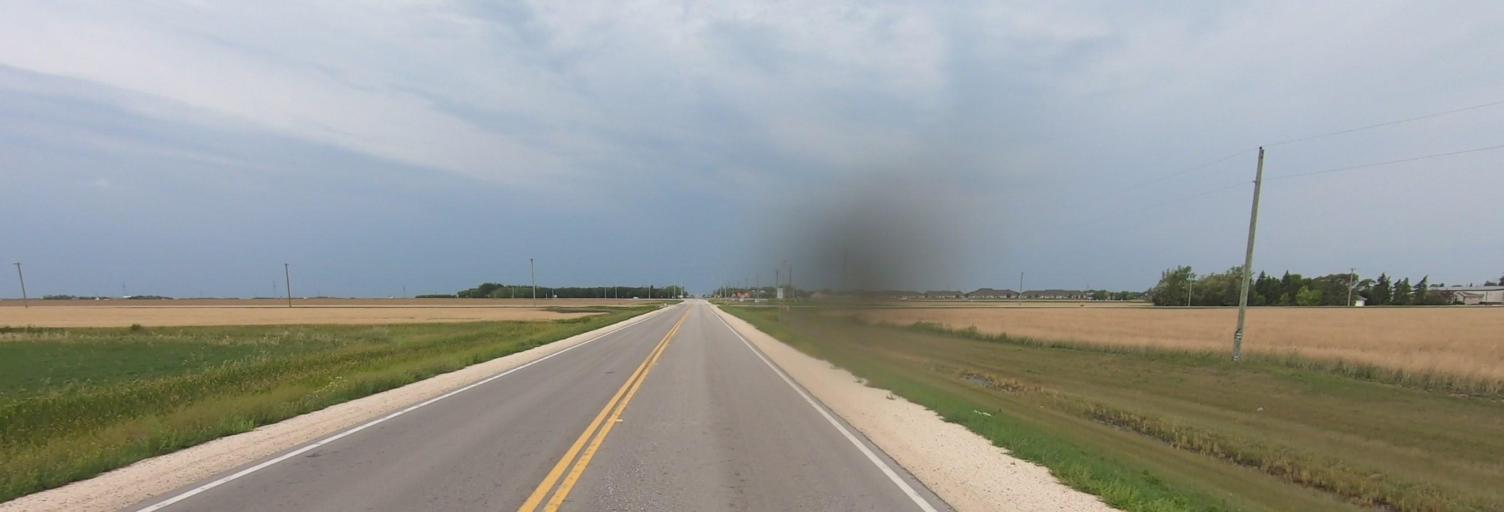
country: CA
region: Manitoba
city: Headingley
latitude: 49.7683
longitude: -97.3192
